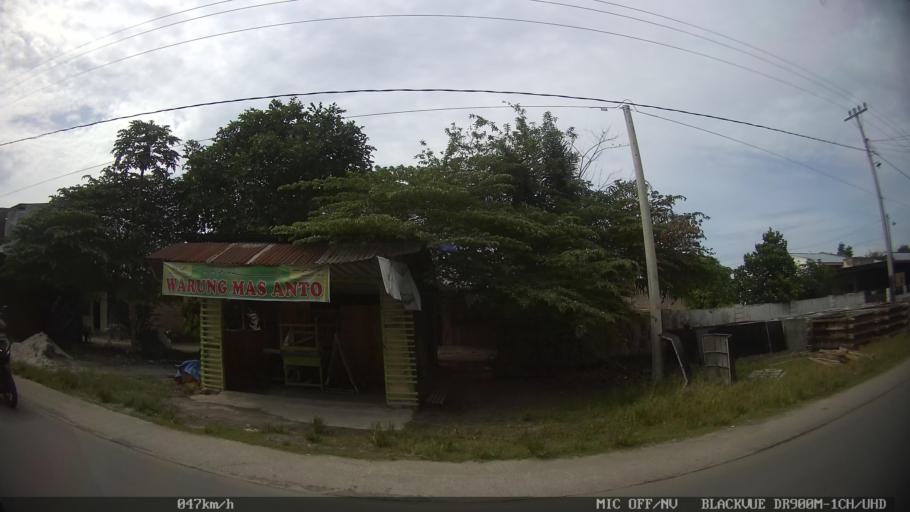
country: ID
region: North Sumatra
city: Percut
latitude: 3.6200
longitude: 98.7648
